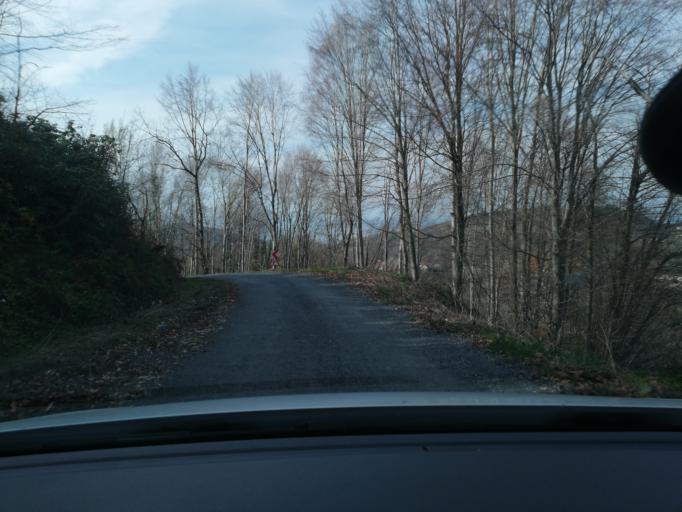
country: TR
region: Zonguldak
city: Kozlu
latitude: 41.3530
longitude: 31.6309
